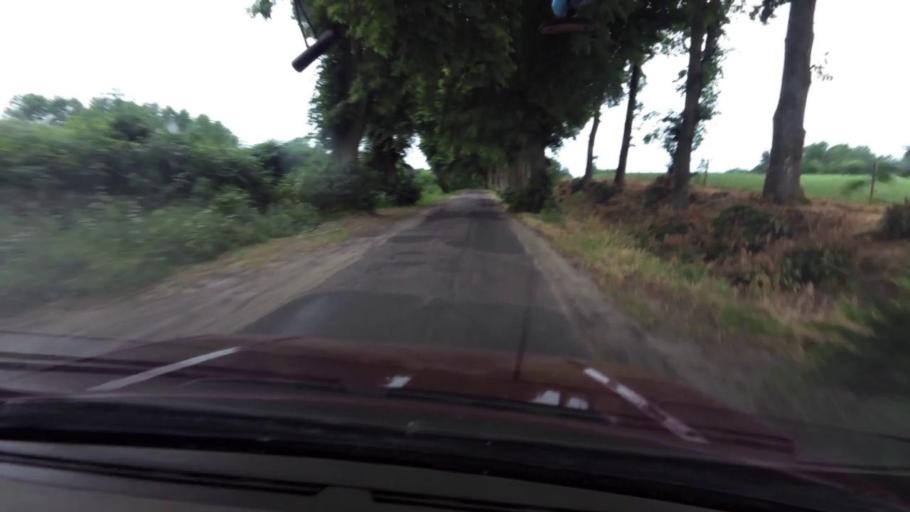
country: PL
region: Pomeranian Voivodeship
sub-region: Powiat slupski
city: Kepice
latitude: 54.1892
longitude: 16.7957
